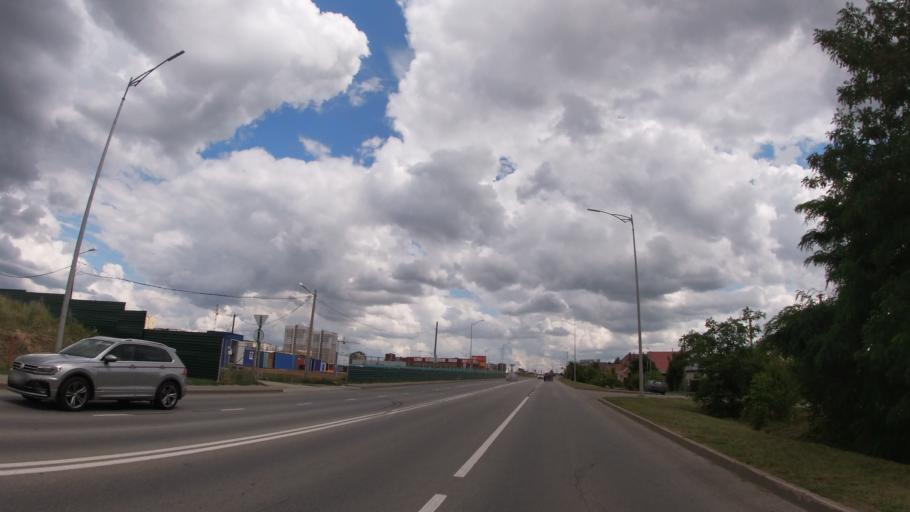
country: RU
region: Belgorod
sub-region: Belgorodskiy Rayon
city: Belgorod
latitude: 50.5509
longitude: 36.5591
